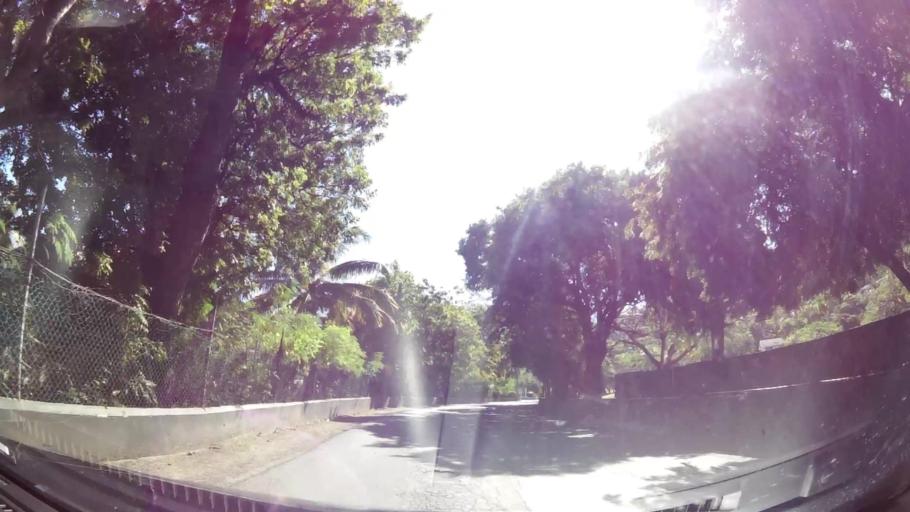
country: VG
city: Road Town
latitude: 18.4094
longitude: -64.6157
